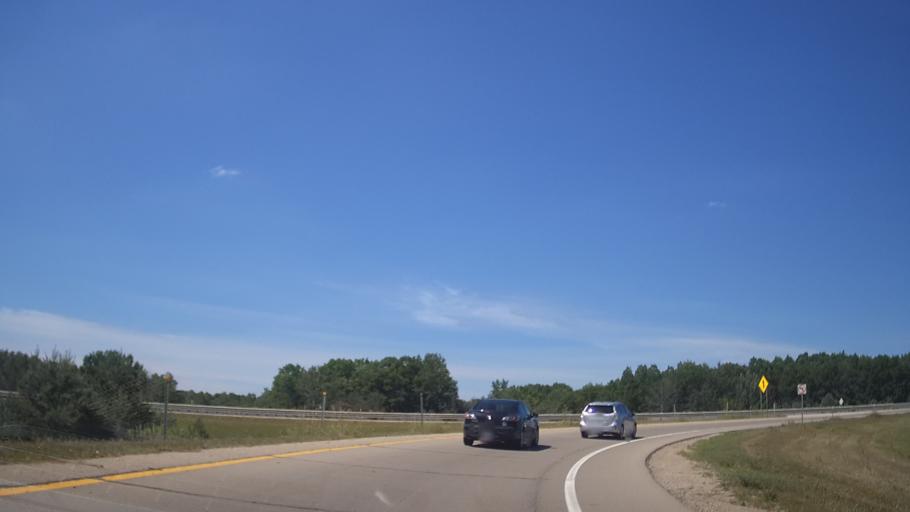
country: US
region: Michigan
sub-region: Clare County
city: Clare
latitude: 43.8634
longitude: -84.9112
